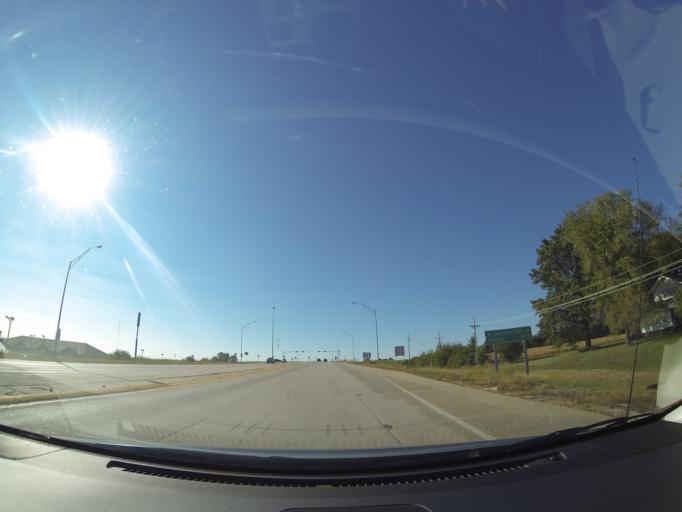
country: US
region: Nebraska
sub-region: Sarpy County
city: Gretna
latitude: 41.0976
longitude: -96.2534
